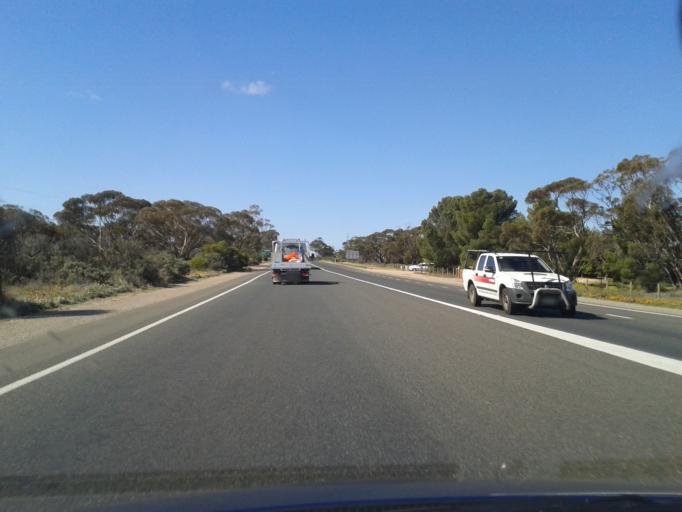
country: AU
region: South Australia
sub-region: Berri and Barmera
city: Berri
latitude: -34.2346
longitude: 140.6461
